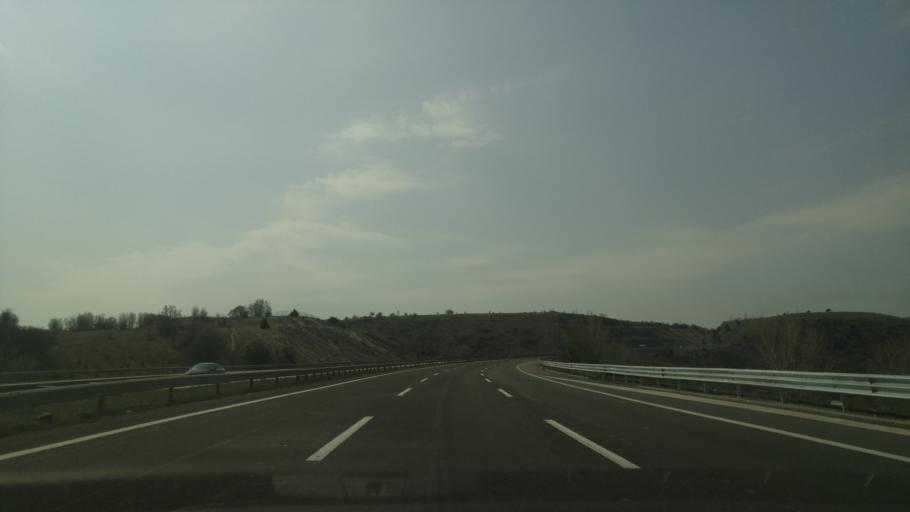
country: TR
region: Ankara
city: Celtikci
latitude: 40.2777
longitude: 32.4858
